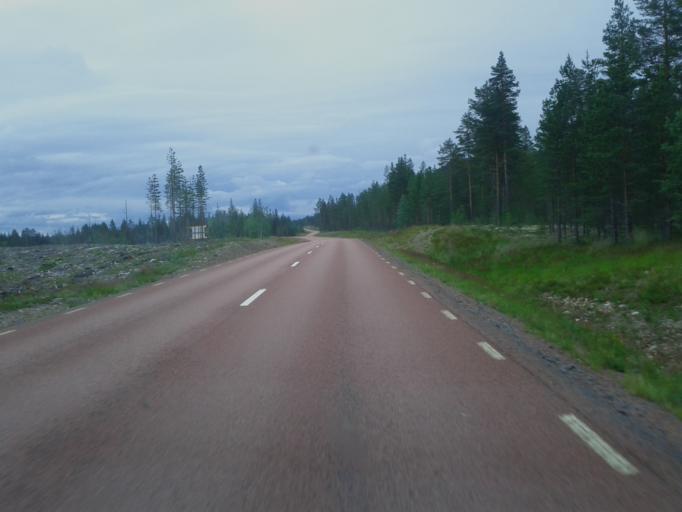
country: NO
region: Hedmark
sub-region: Trysil
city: Innbygda
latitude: 61.6771
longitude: 13.1668
